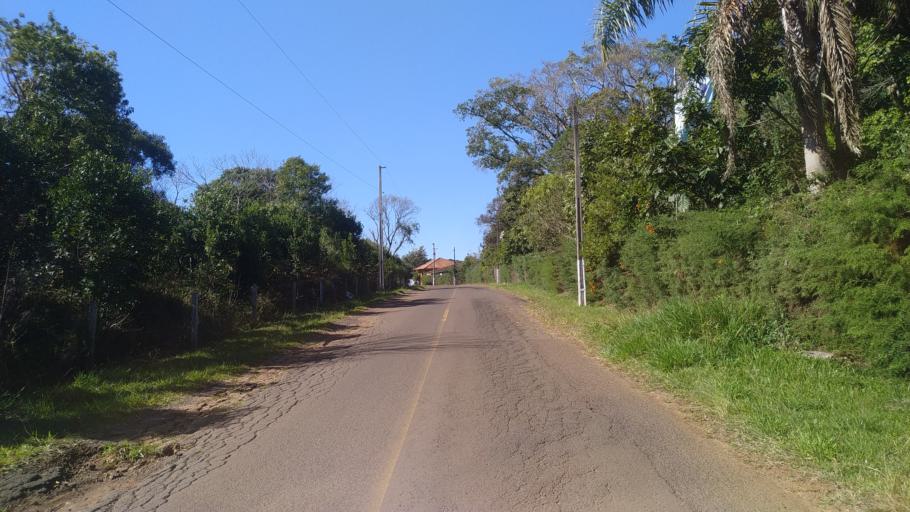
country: BR
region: Santa Catarina
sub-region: Chapeco
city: Chapeco
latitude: -27.1493
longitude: -52.6180
